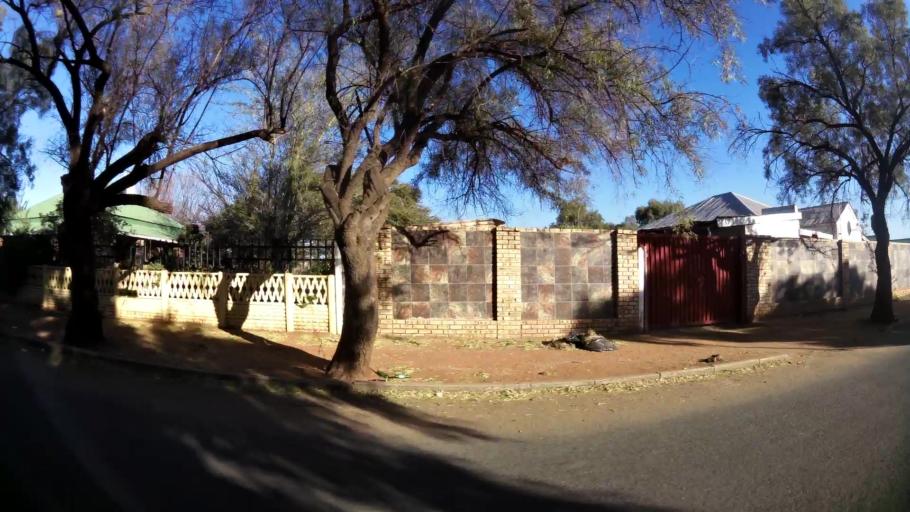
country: ZA
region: Northern Cape
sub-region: Frances Baard District Municipality
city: Kimberley
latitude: -28.7362
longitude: 24.7436
